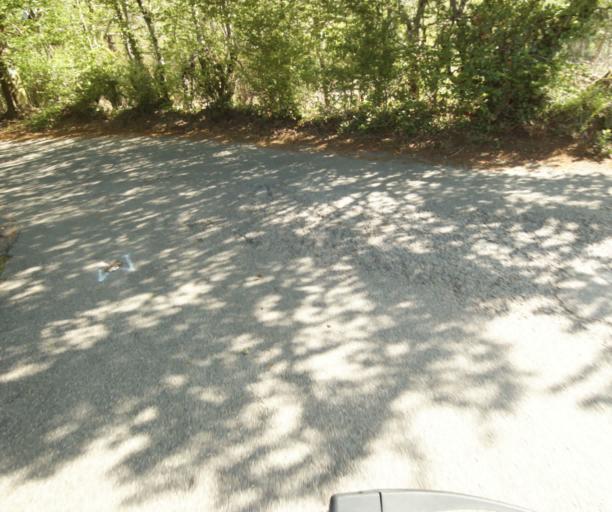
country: FR
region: Limousin
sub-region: Departement de la Correze
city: Tulle
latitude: 45.2670
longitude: 1.7789
